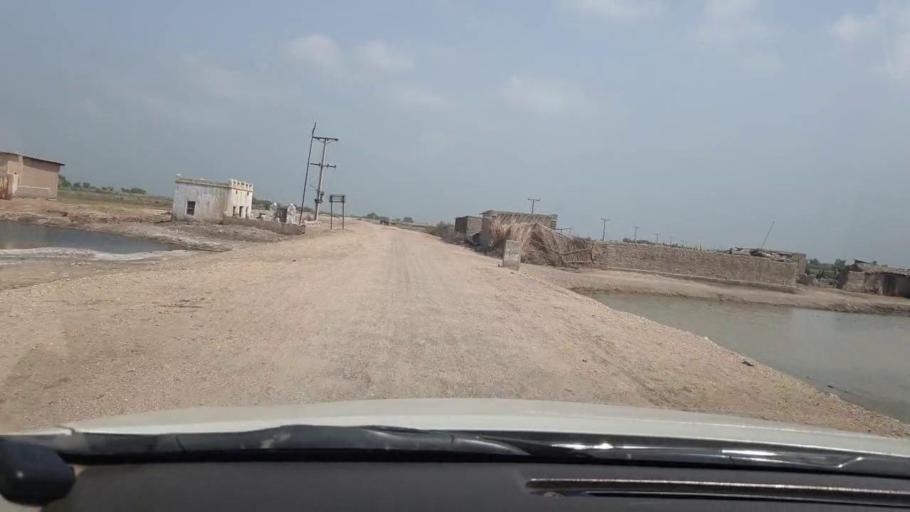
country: PK
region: Sindh
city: Shikarpur
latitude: 28.0072
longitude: 68.5573
